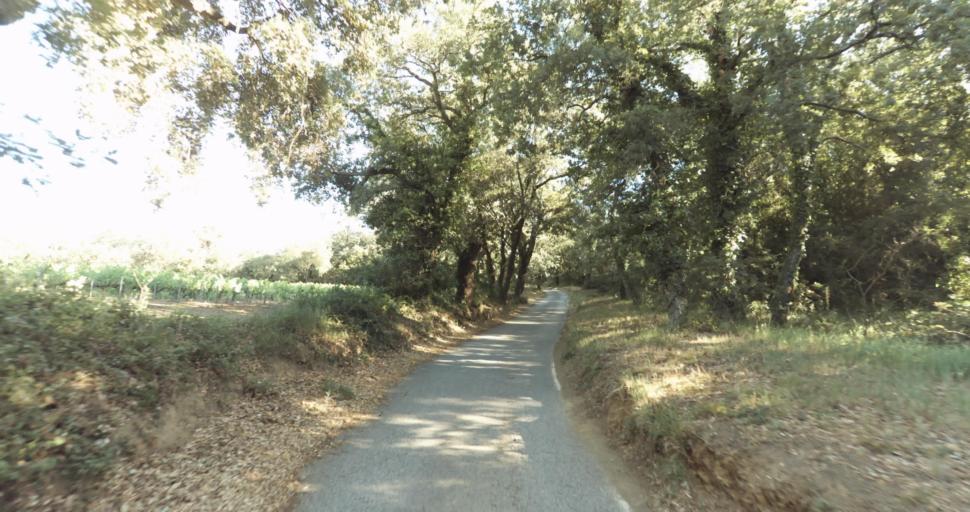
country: FR
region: Provence-Alpes-Cote d'Azur
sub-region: Departement du Var
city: Gassin
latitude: 43.2321
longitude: 6.5884
